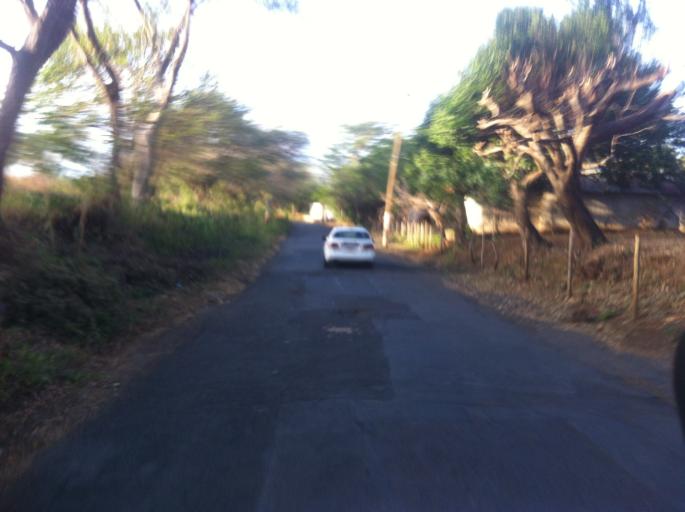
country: NI
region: Managua
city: Ciudad Sandino
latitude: 12.1063
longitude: -86.3133
